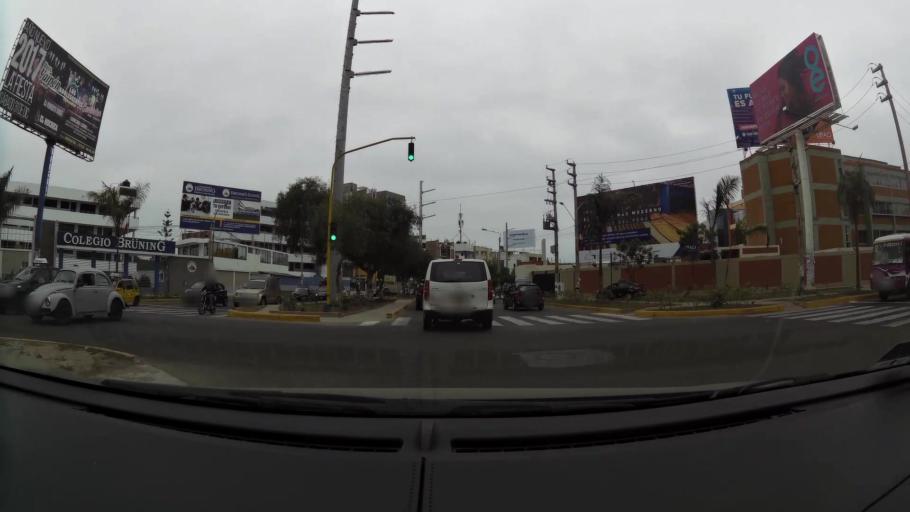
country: PE
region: La Libertad
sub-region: Provincia de Trujillo
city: Trujillo
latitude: -8.1267
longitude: -79.0305
